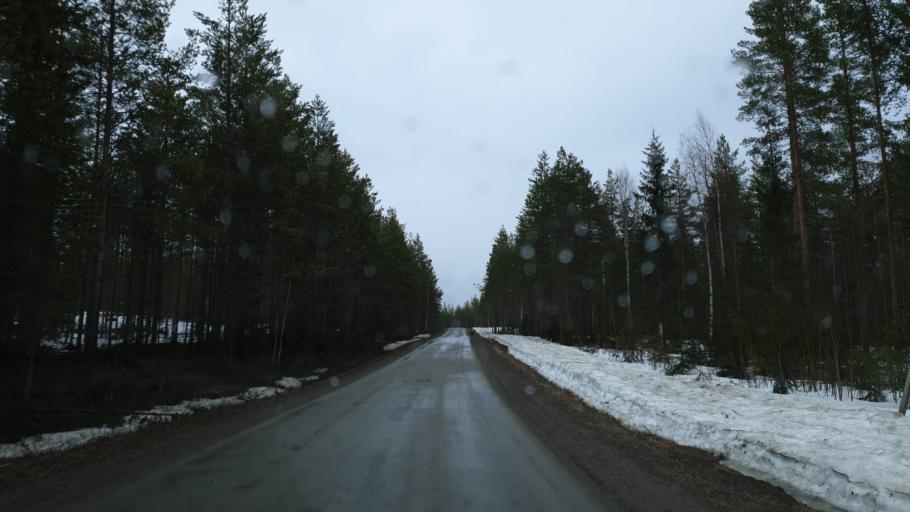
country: SE
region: Vaesterbotten
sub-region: Skelleftea Kommun
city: Byske
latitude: 64.8821
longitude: 21.1390
